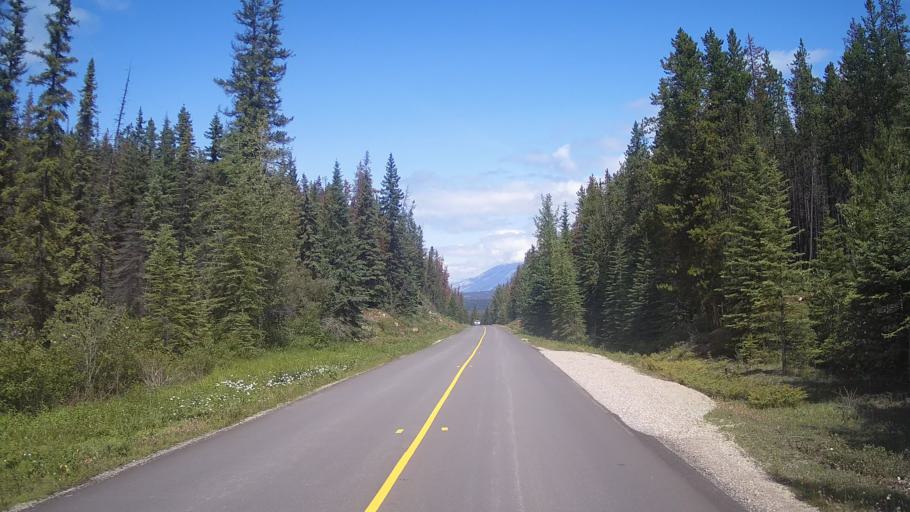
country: CA
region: Alberta
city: Jasper Park Lodge
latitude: 52.7813
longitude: -118.0325
